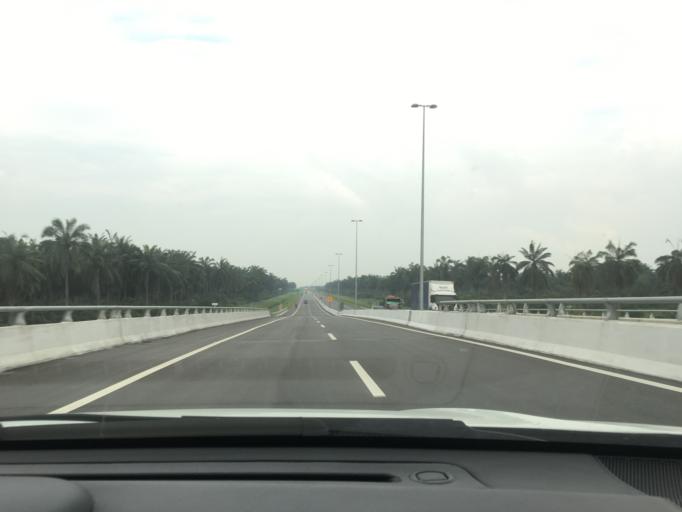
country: MY
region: Selangor
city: Klang
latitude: 3.1133
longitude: 101.4121
